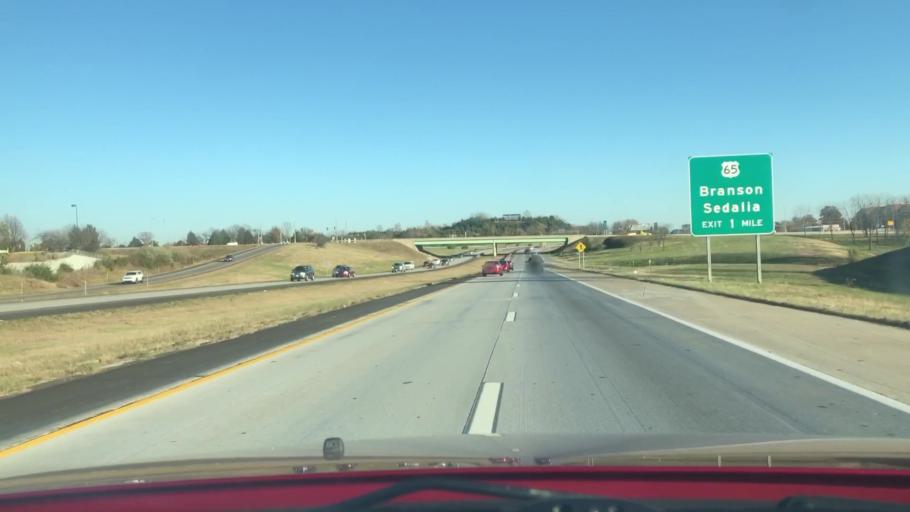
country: US
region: Missouri
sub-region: Greene County
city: Springfield
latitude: 37.1398
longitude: -93.2570
